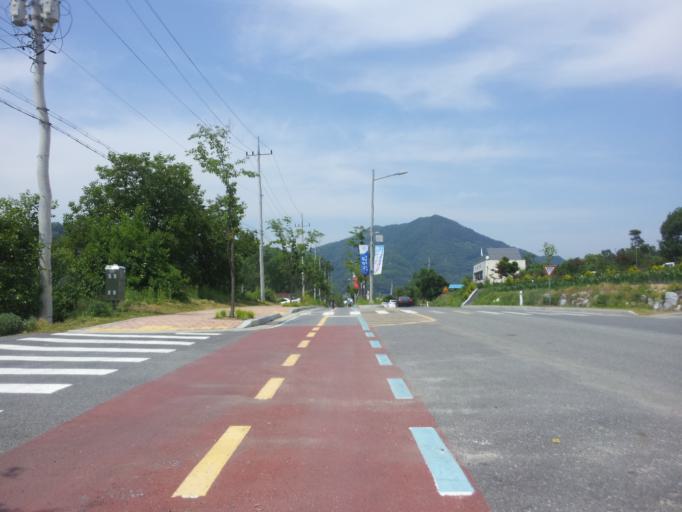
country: KR
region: Daejeon
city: Sintansin
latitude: 36.4630
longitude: 127.4666
